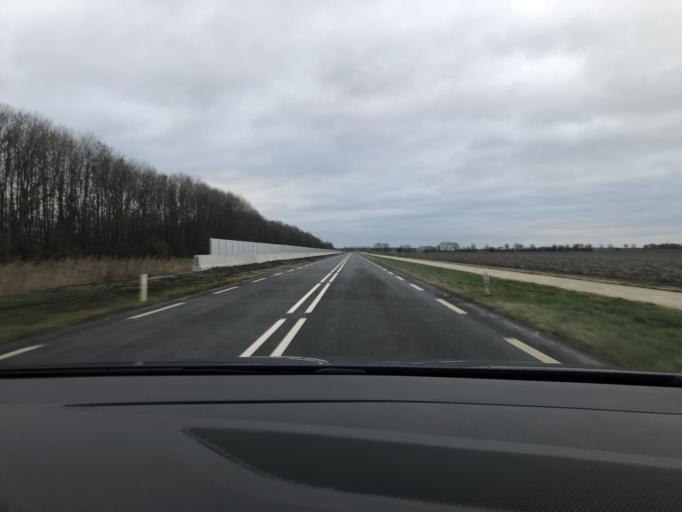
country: NL
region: Flevoland
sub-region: Gemeente Lelystad
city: Lelystad
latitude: 52.4601
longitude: 5.5105
